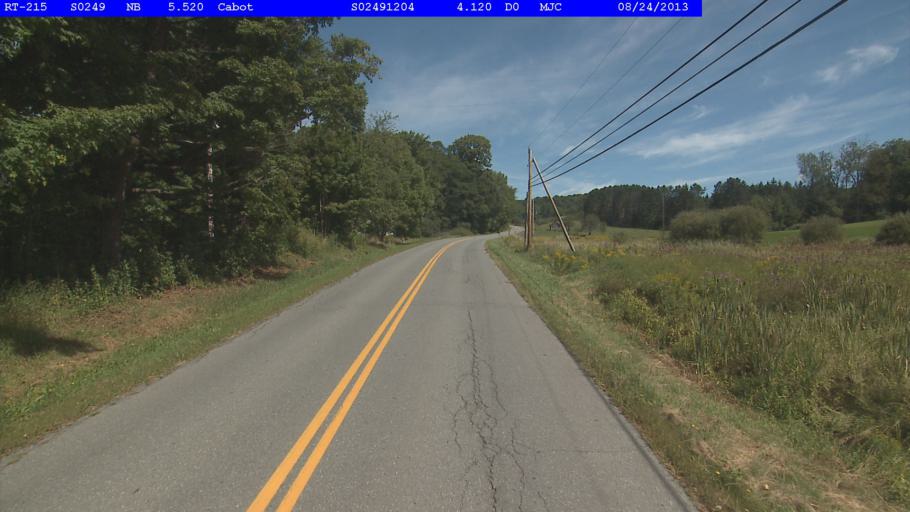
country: US
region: Vermont
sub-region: Caledonia County
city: Hardwick
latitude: 44.4149
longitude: -72.3010
